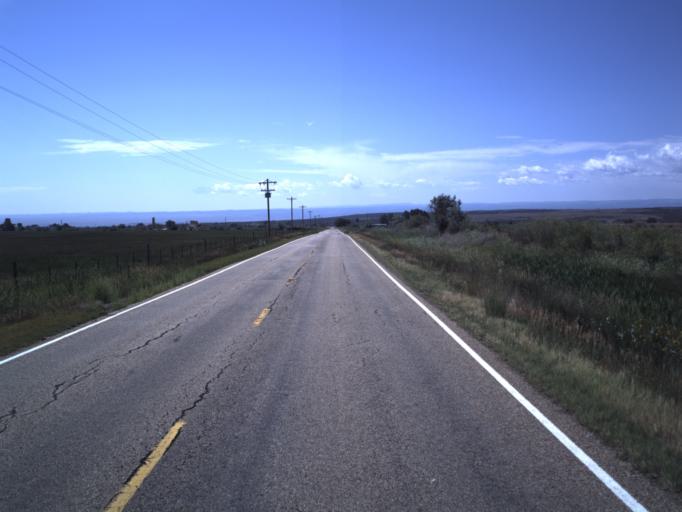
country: US
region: Utah
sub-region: Duchesne County
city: Duchesne
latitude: 40.3428
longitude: -110.2752
